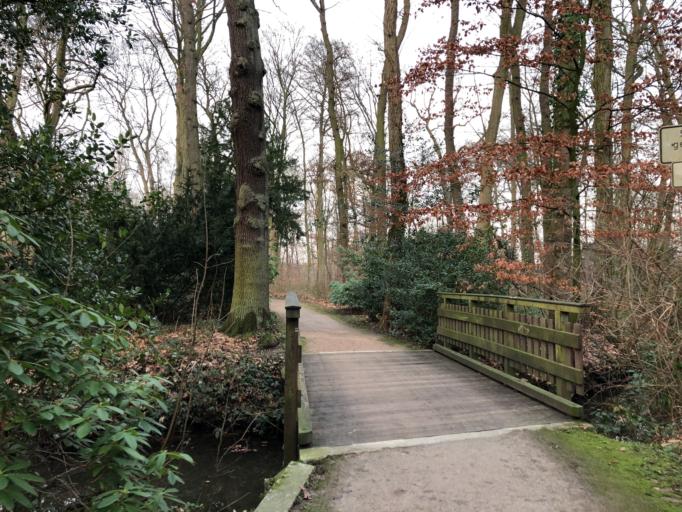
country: DE
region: North Rhine-Westphalia
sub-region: Regierungsbezirk Dusseldorf
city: Erkrath
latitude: 51.1952
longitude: 6.8513
